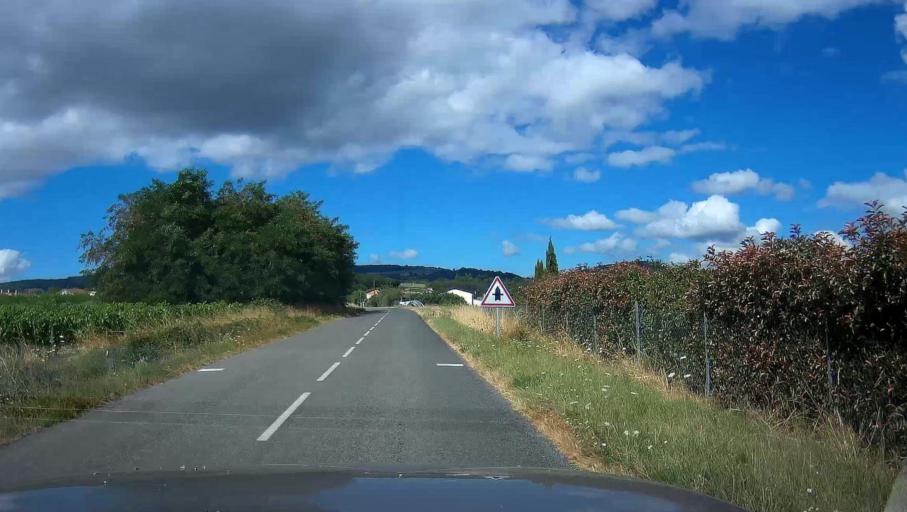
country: FR
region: Rhone-Alpes
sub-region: Departement du Rhone
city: Cogny
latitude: 45.9751
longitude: 4.6316
